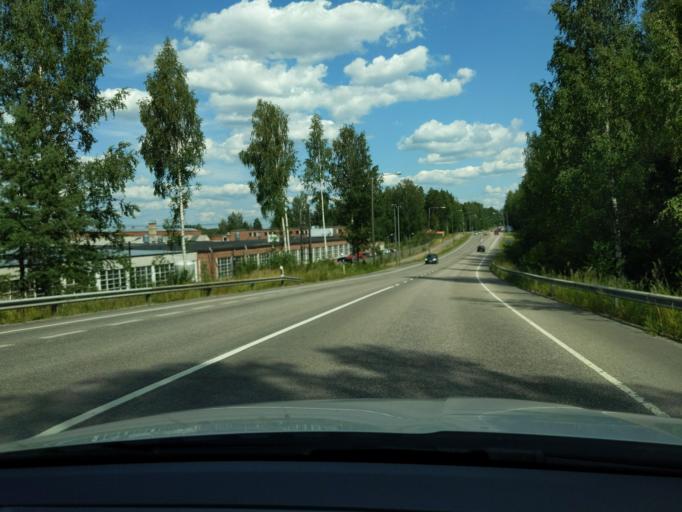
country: FI
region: Paijanne Tavastia
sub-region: Lahti
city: Heinola
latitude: 61.1932
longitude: 26.0077
